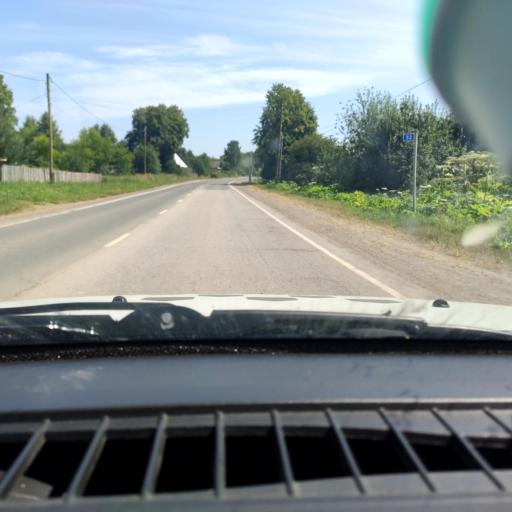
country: RU
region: Perm
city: Okhansk
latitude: 57.7016
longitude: 55.2657
